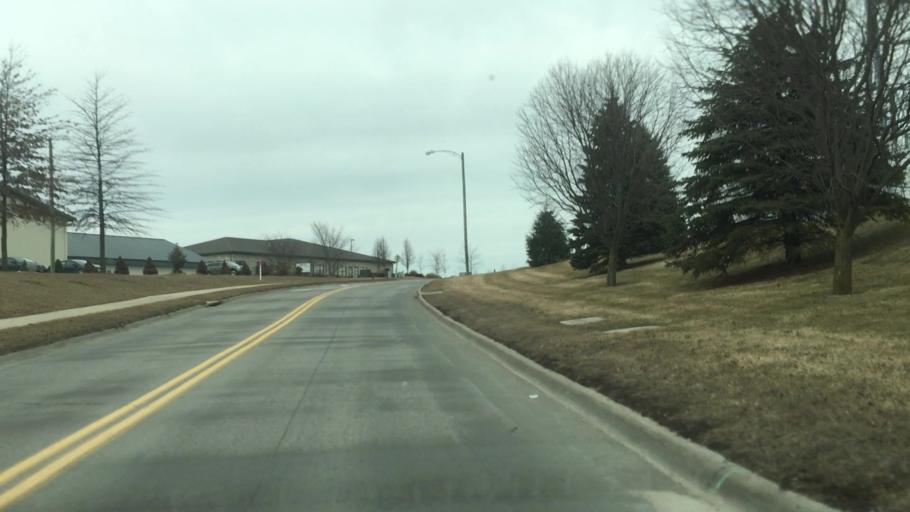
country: US
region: Iowa
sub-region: Johnson County
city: Coralville
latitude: 41.7014
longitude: -91.5872
